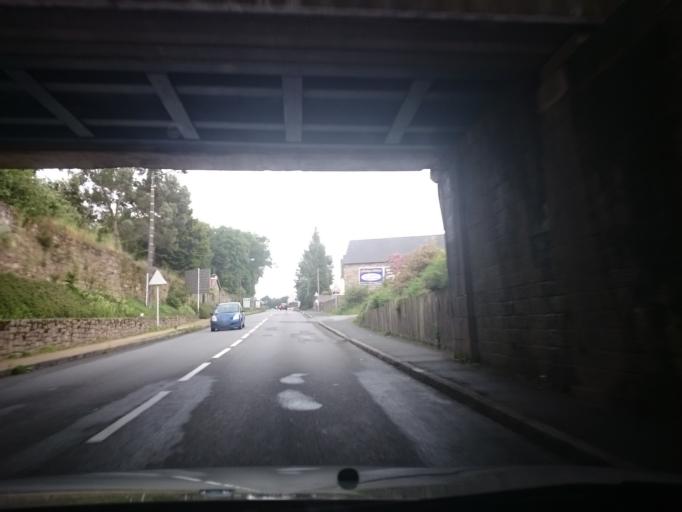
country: FR
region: Brittany
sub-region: Departement des Cotes-d'Armor
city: Guingamp
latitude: 48.5544
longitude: -3.1499
